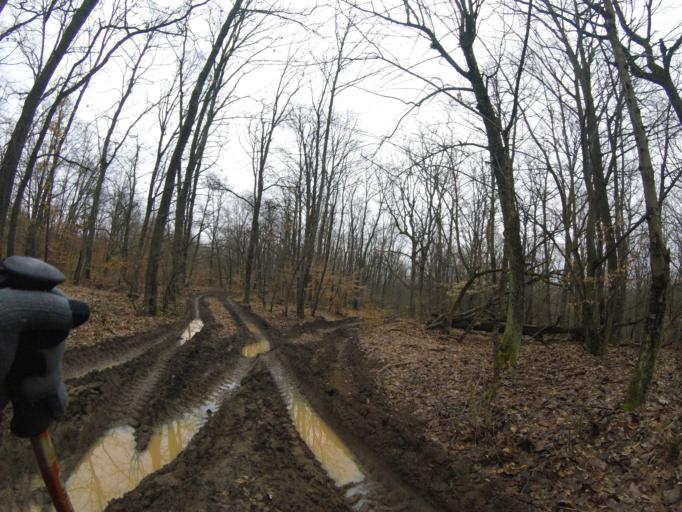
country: HU
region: Borsod-Abauj-Zemplen
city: Rudabanya
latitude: 48.4559
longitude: 20.5821
